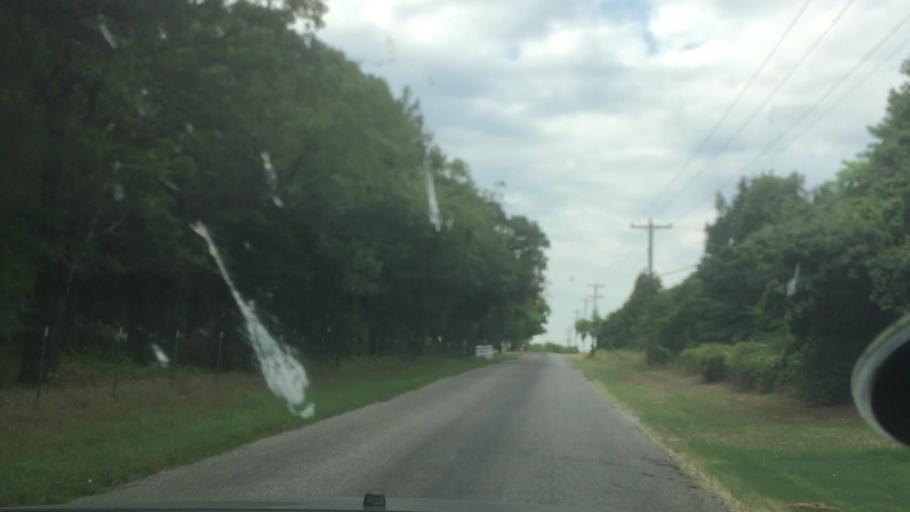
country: US
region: Texas
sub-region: Grayson County
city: Pottsboro
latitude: 33.8115
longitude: -96.7031
